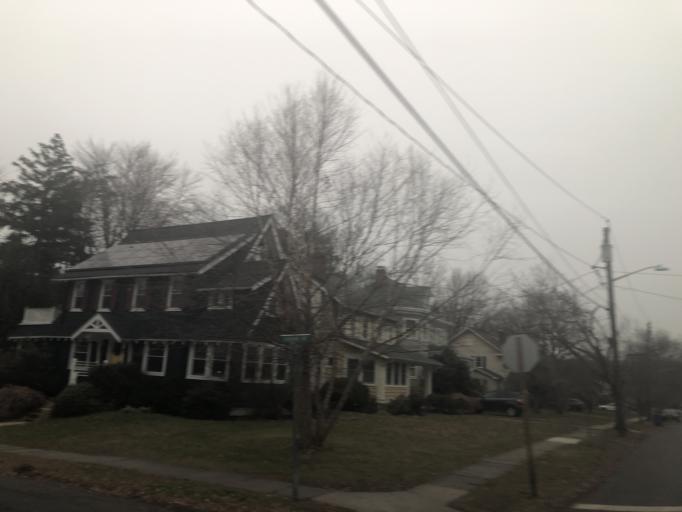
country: US
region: New Jersey
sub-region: Essex County
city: Maplewood
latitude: 40.7229
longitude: -74.2687
